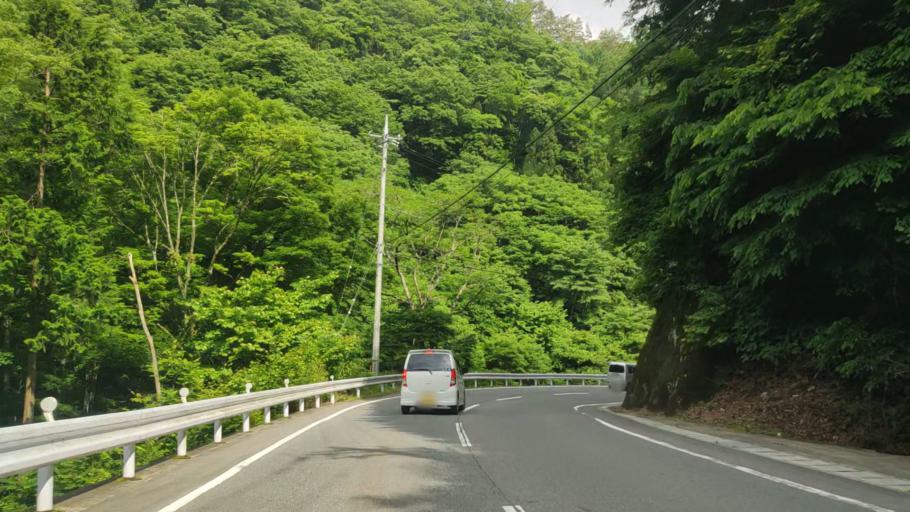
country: JP
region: Gunma
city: Tomioka
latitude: 36.1004
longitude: 138.7177
